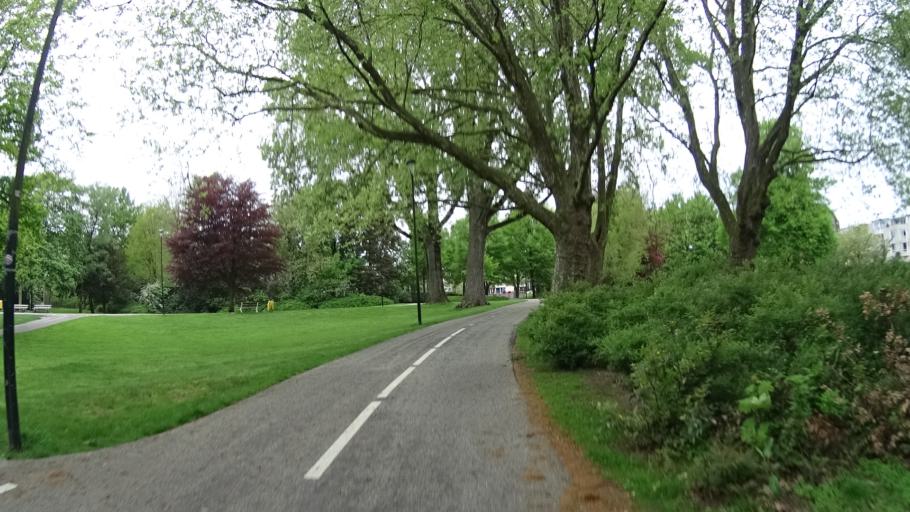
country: NL
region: North Brabant
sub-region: Gemeente Veghel
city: Veghel
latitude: 51.6142
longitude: 5.5431
